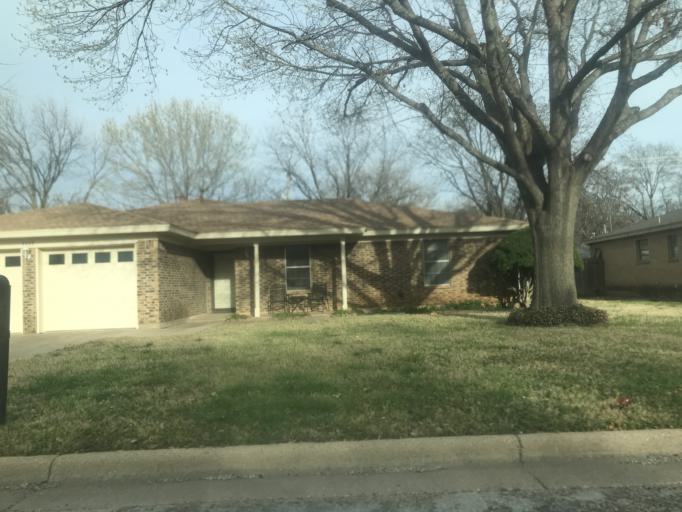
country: US
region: Texas
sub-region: Taylor County
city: Abilene
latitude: 32.3934
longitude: -99.7705
